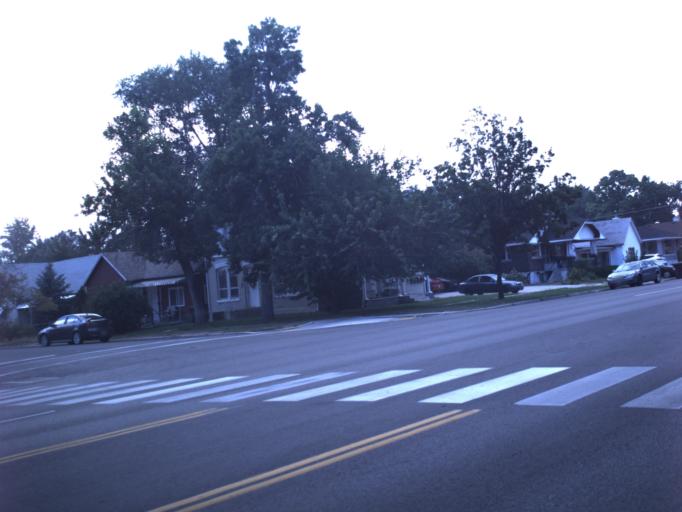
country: US
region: Utah
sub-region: Utah County
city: Provo
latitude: 40.2309
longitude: -111.6674
